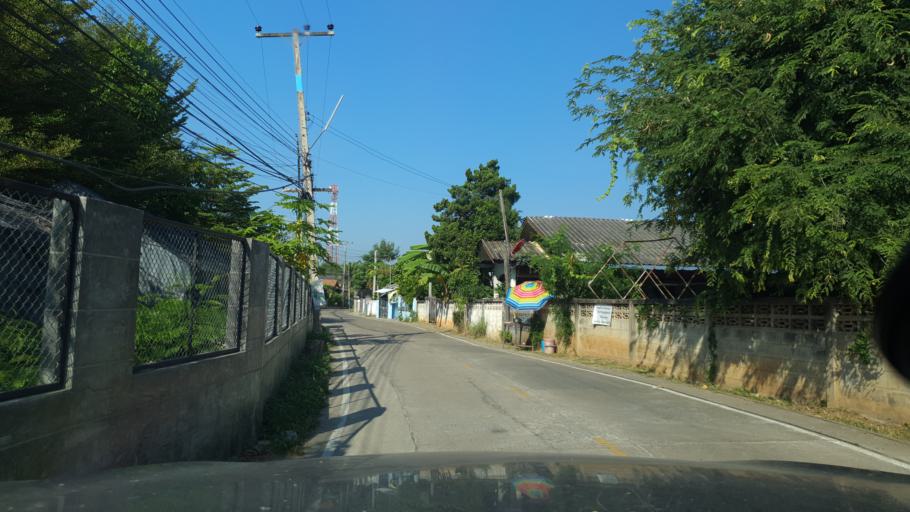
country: TH
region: Chiang Mai
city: Hang Dong
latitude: 18.7112
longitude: 98.9443
